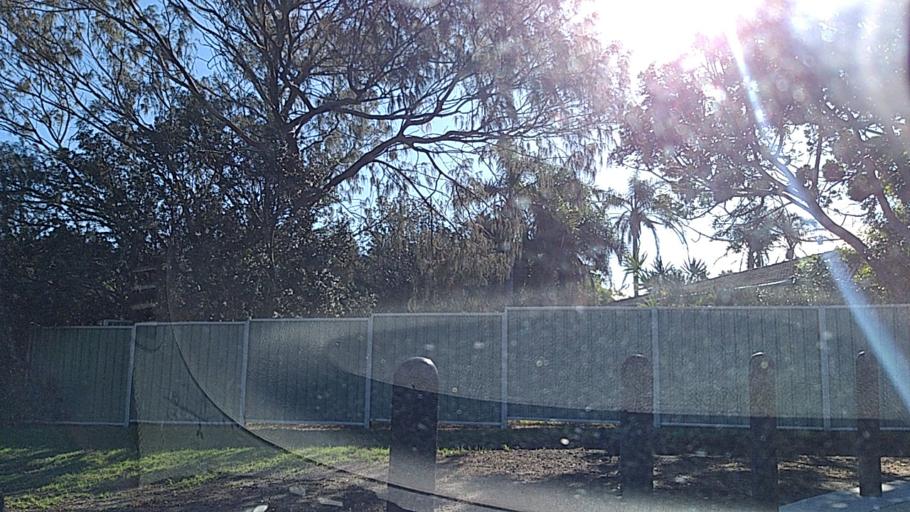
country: AU
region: New South Wales
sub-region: Wollongong
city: East Corrimal
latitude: -34.3810
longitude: 150.9150
